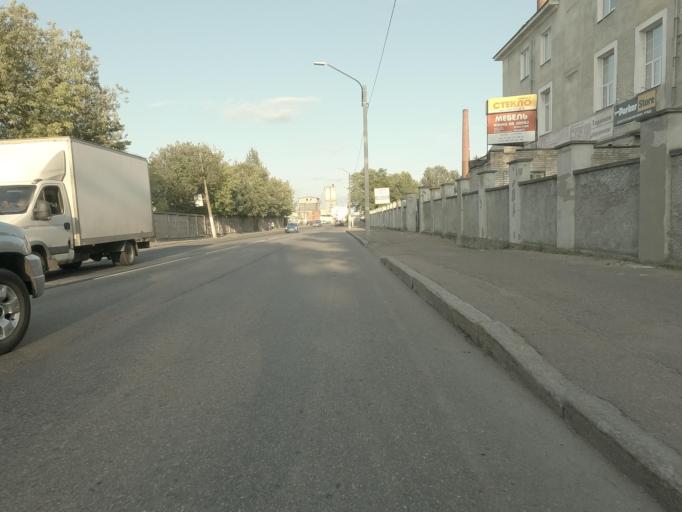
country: RU
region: Leningrad
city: Vyborg
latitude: 60.7107
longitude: 28.7674
